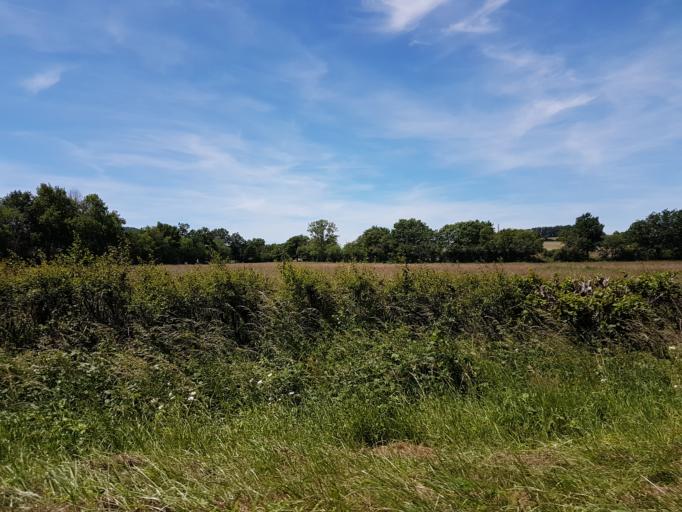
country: FR
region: Bourgogne
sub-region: Departement de Saone-et-Loire
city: Epinac
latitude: 46.9899
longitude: 4.4837
